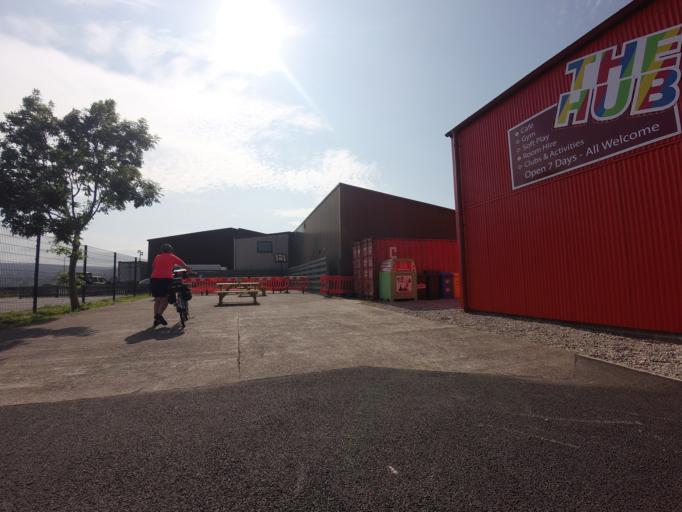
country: GB
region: Scotland
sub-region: Highland
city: Alness
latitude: 57.8906
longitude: -4.3516
